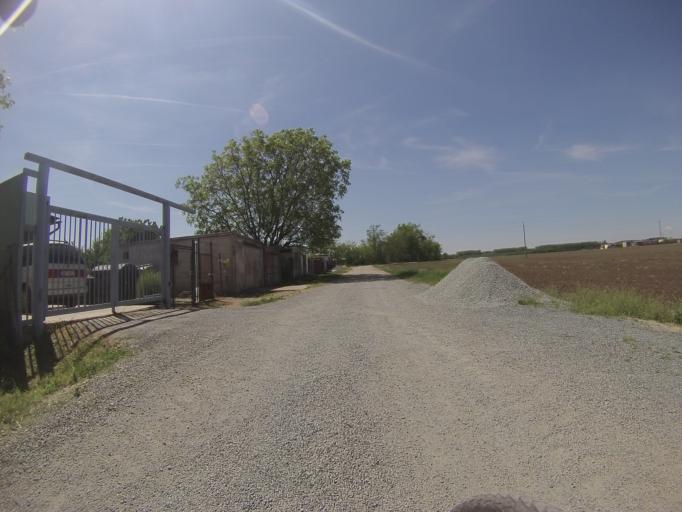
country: CZ
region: South Moravian
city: Zabcice
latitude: 49.0061
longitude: 16.6073
